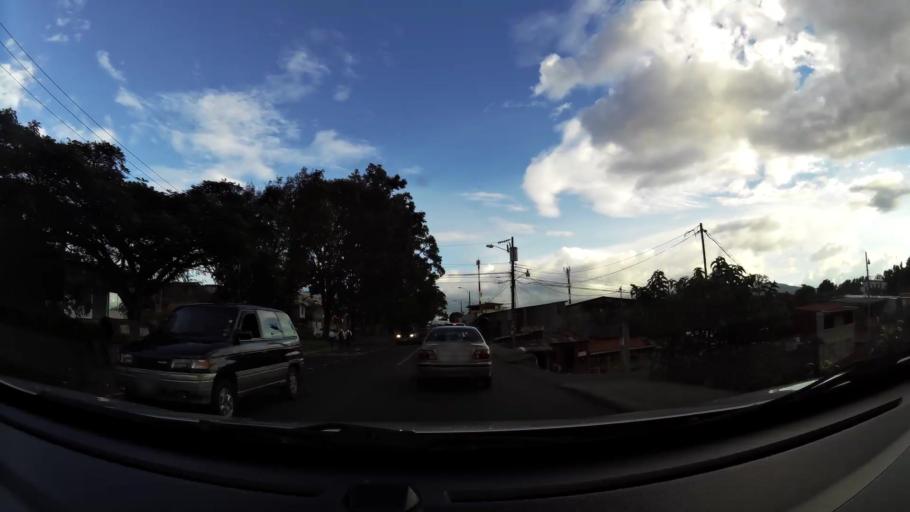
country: CR
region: Alajuela
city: Alajuela
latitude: 10.0078
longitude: -84.2072
